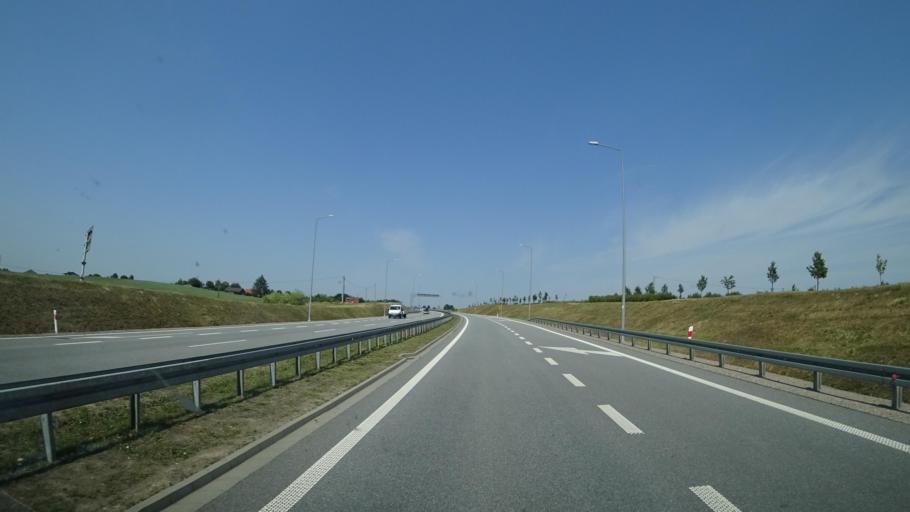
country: PL
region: Pomeranian Voivodeship
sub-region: Powiat koscierski
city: Koscierzyna
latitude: 54.1258
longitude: 18.0190
